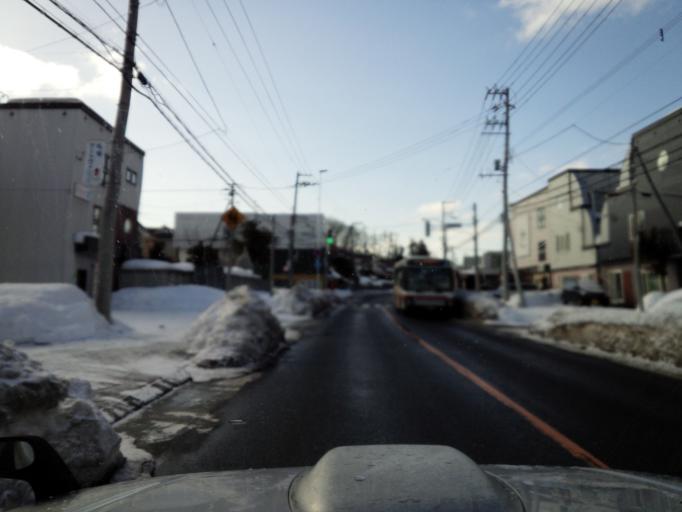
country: JP
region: Hokkaido
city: Sapporo
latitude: 42.9467
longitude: 141.3469
